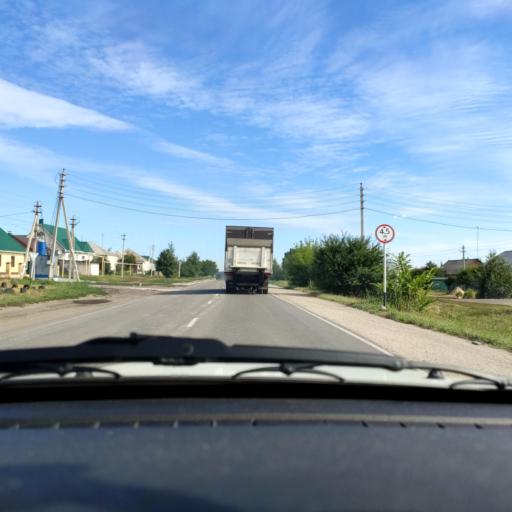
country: RU
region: Voronezj
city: Orlovo
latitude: 51.7548
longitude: 39.5880
